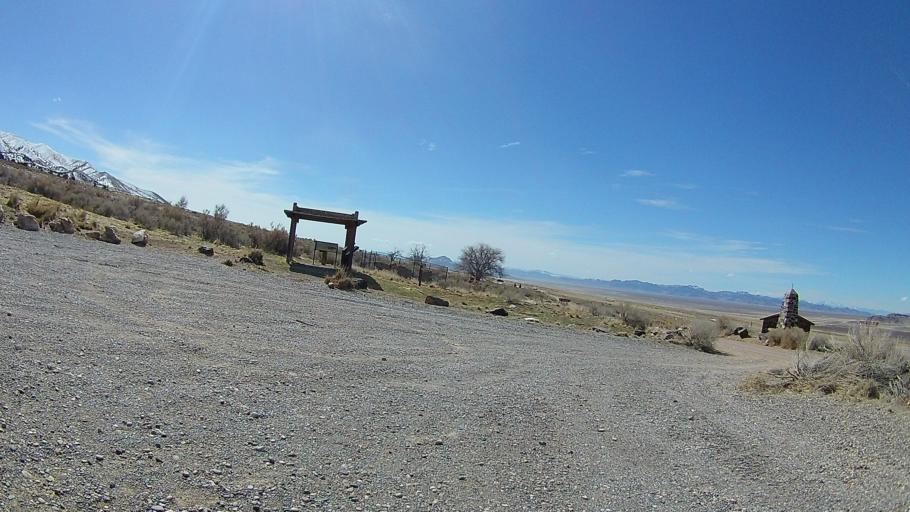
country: US
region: Utah
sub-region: Tooele County
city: Grantsville
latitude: 40.0396
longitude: -112.7870
